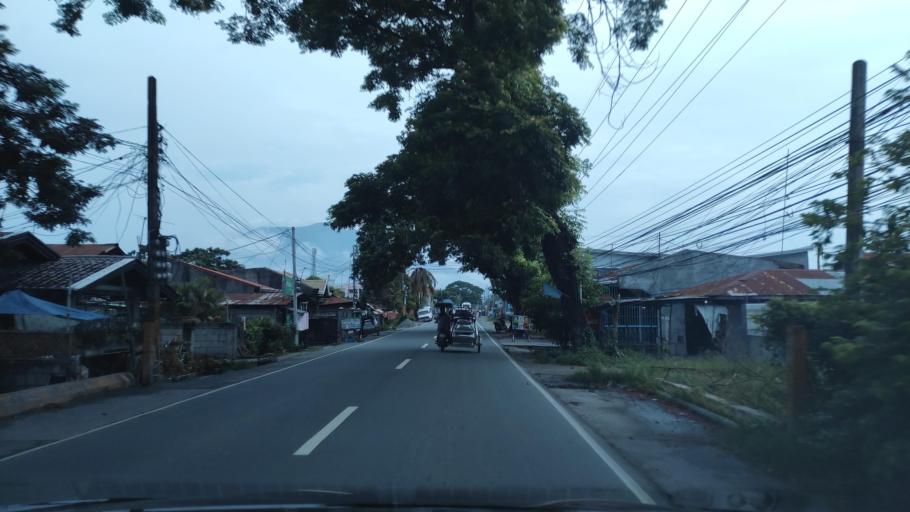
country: PH
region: Central Luzon
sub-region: Province of Pampanga
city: Arayat
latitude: 15.1350
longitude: 120.7741
